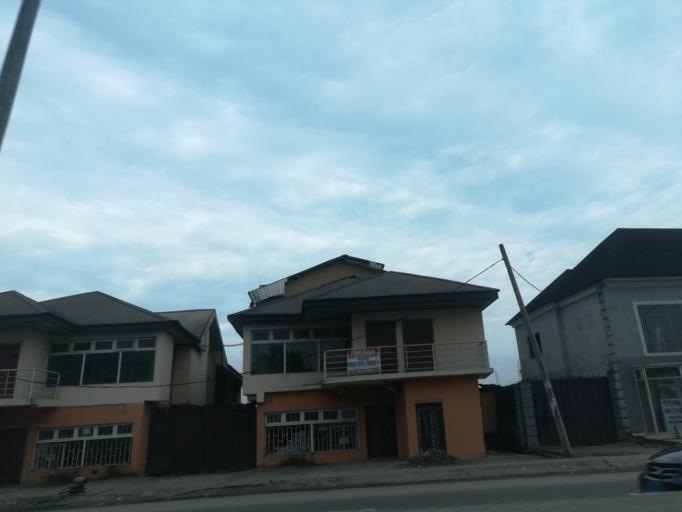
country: NG
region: Rivers
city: Port Harcourt
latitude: 4.8388
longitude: 6.9759
